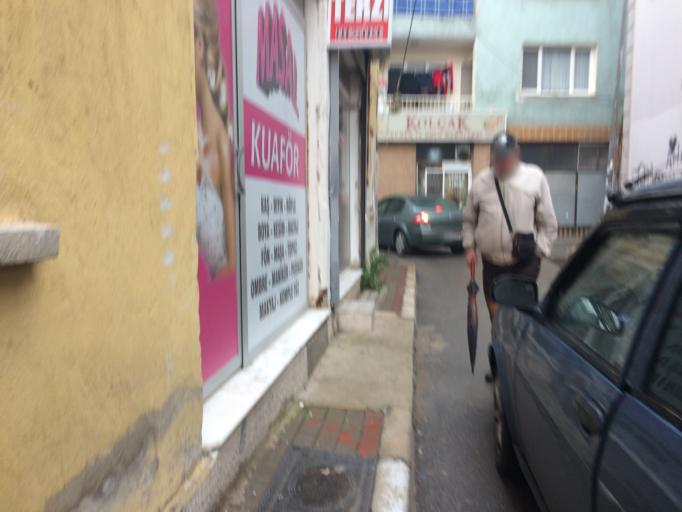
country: TR
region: Izmir
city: Karsiyaka
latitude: 38.4928
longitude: 27.0650
